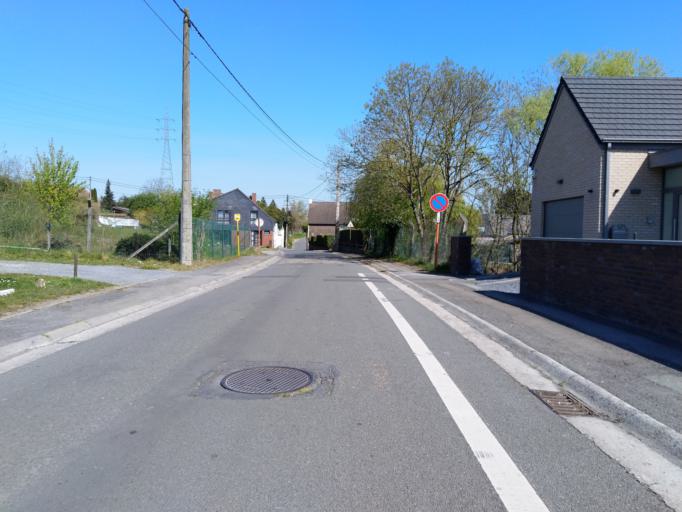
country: BE
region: Wallonia
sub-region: Province du Hainaut
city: Mons
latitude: 50.4771
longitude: 4.0067
